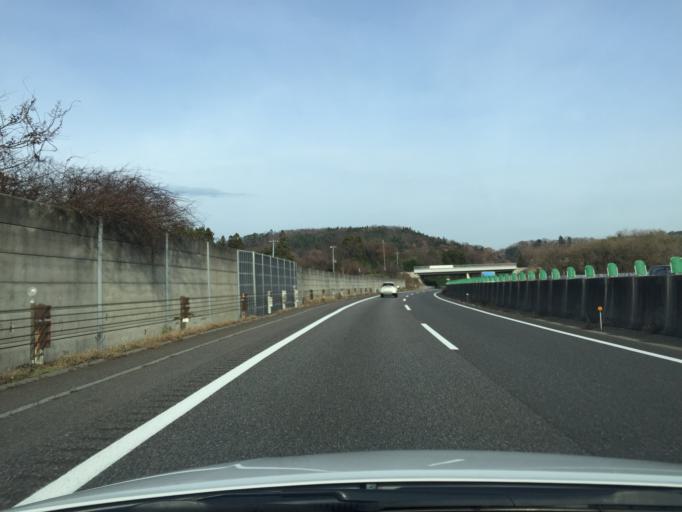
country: JP
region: Fukushima
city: Nihommatsu
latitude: 37.6193
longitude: 140.4242
